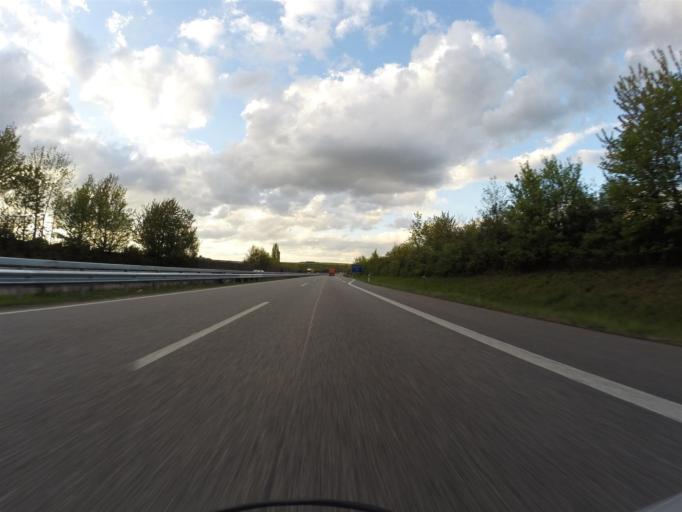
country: DE
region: Rheinland-Pfalz
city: Kirchheimbolanden
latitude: 49.6639
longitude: 8.0247
